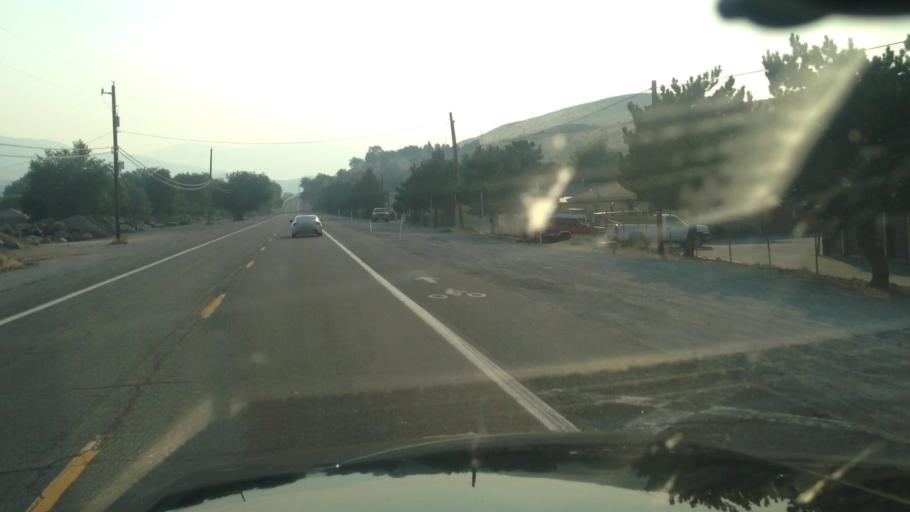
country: US
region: Nevada
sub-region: Washoe County
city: Reno
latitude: 39.5120
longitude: -119.8641
